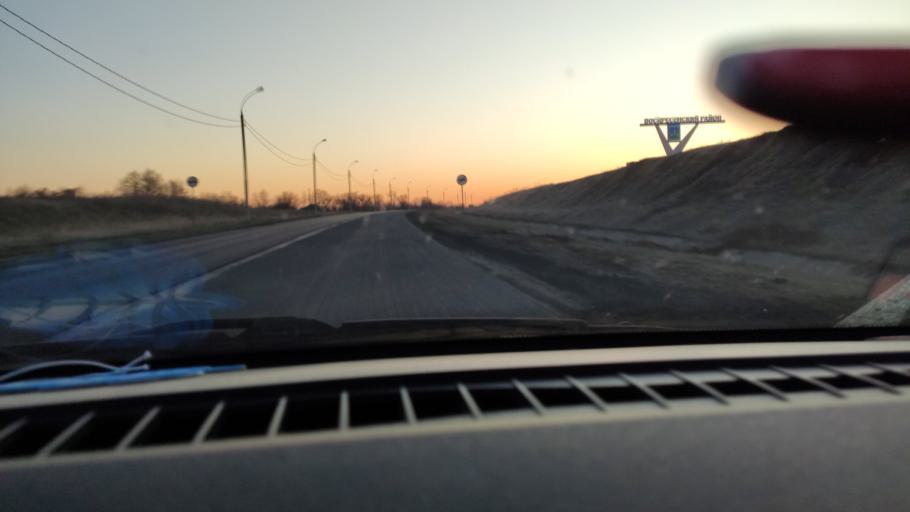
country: RU
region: Saratov
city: Yelshanka
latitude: 51.8272
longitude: 46.2233
